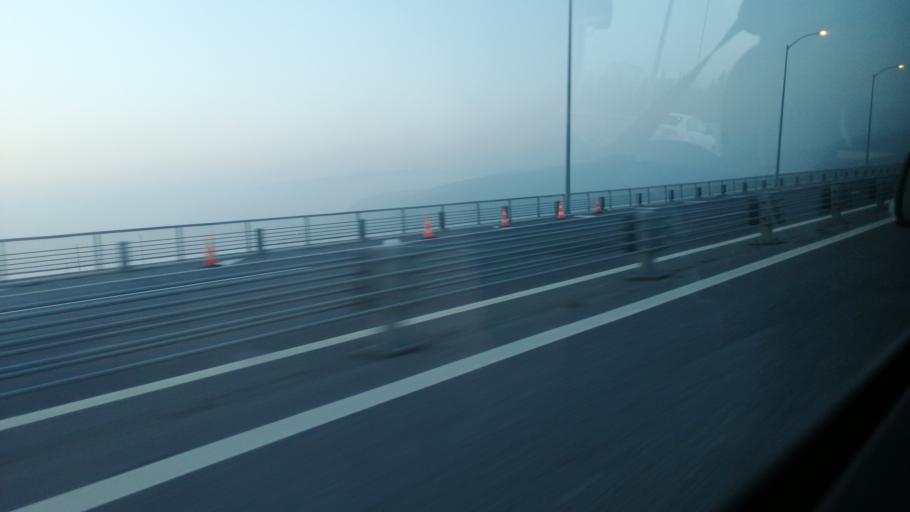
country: TR
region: Kocaeli
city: Tavsanli
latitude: 40.7686
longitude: 29.5181
